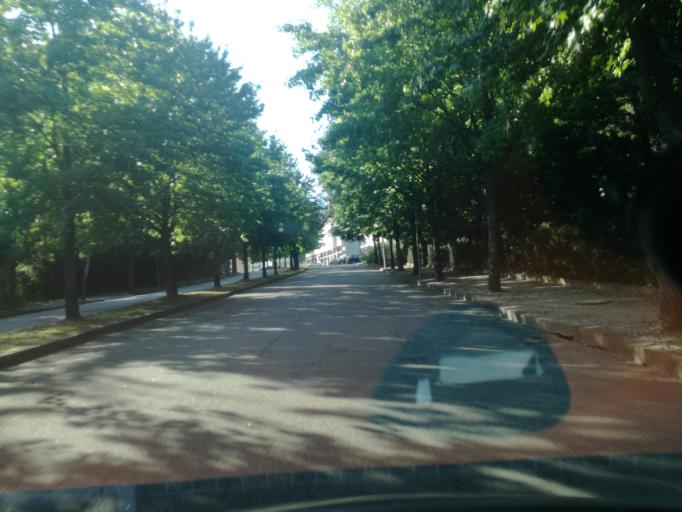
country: PT
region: Porto
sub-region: Maia
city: Gemunde
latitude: 41.2488
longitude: -8.6543
